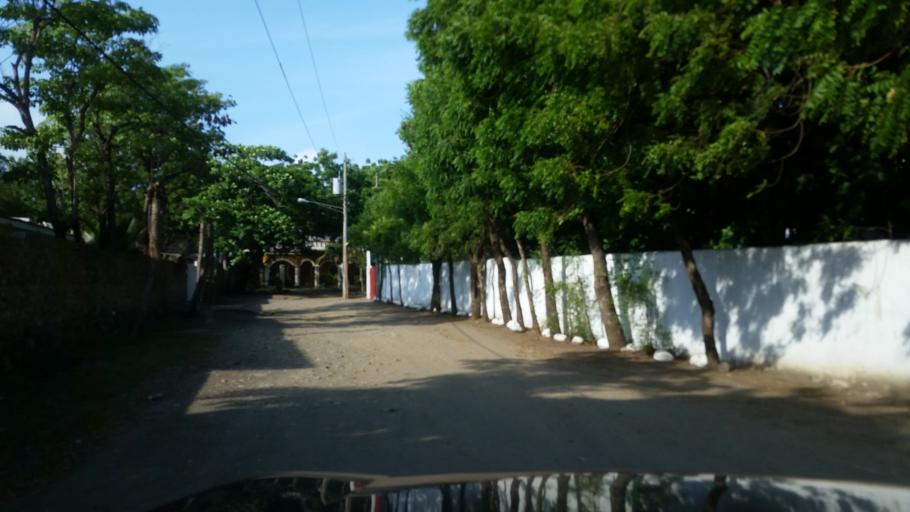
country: NI
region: Managua
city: Masachapa
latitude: 11.7746
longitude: -86.5130
